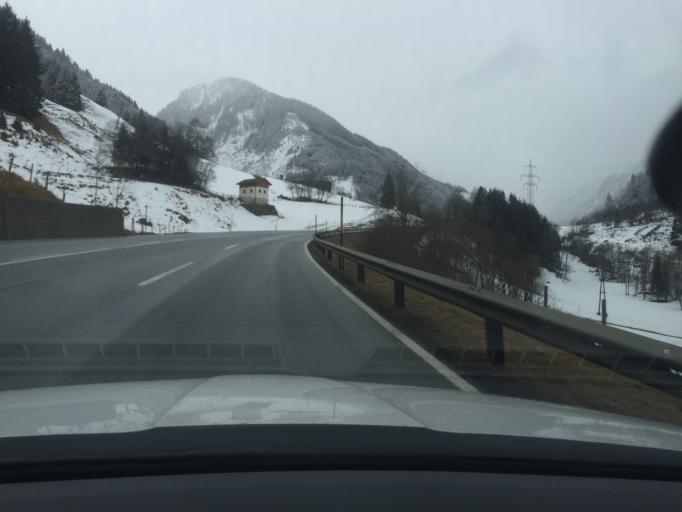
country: AT
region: Salzburg
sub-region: Politischer Bezirk Zell am See
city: Mittersill
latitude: 47.2348
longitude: 12.4941
